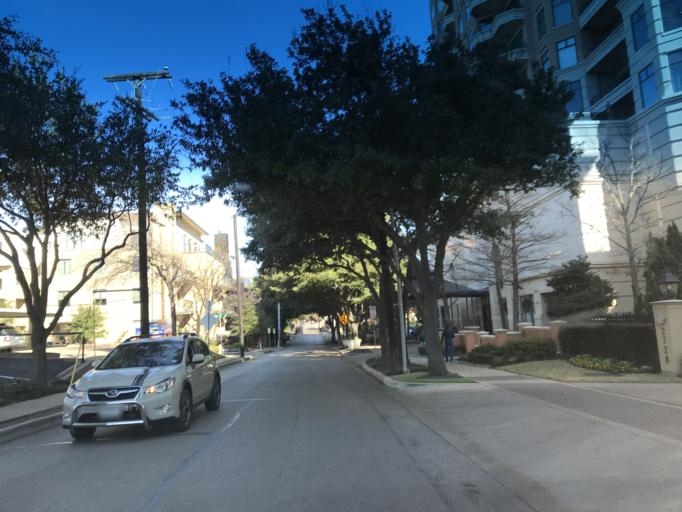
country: US
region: Texas
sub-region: Dallas County
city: Dallas
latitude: 32.8051
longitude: -96.8098
